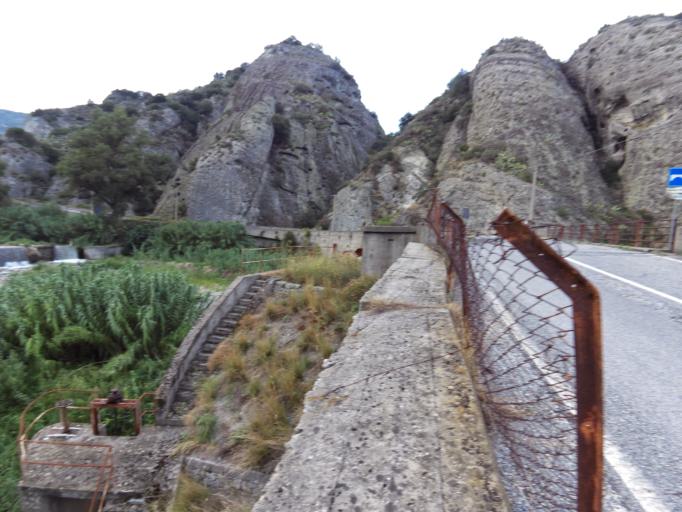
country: IT
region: Calabria
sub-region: Provincia di Reggio Calabria
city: Caulonia
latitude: 38.4030
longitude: 16.4110
